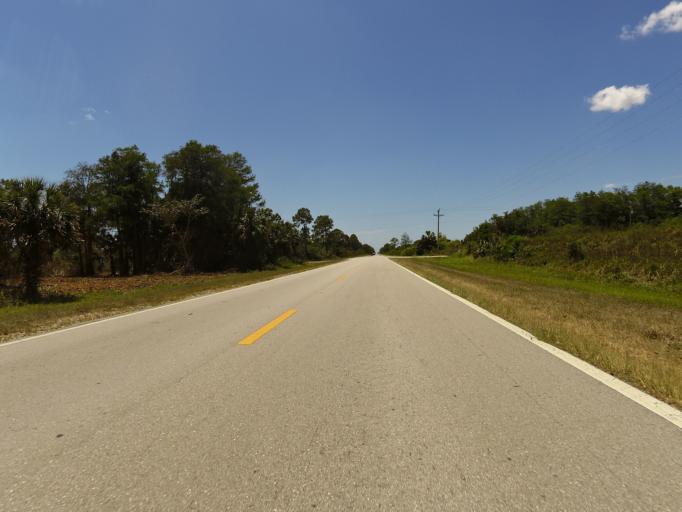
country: US
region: Florida
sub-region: Collier County
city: Immokalee
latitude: 26.2951
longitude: -81.3987
